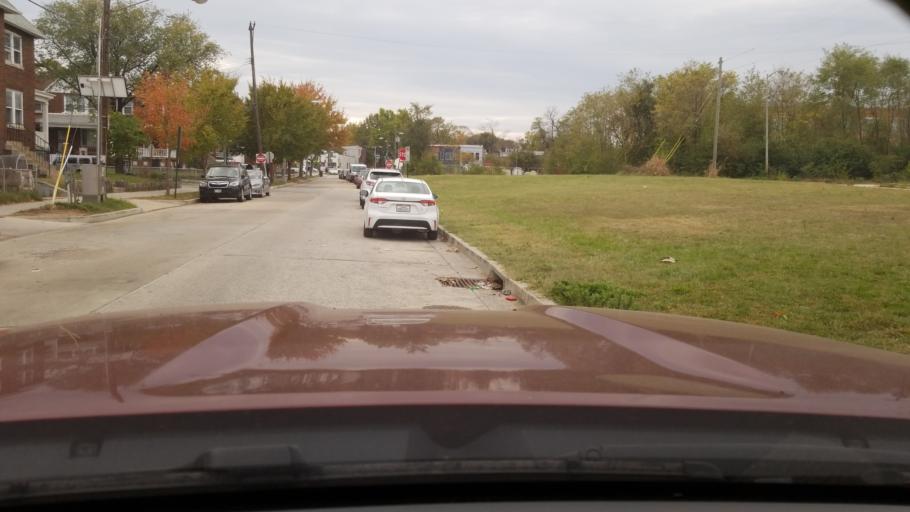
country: US
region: Maryland
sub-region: Prince George's County
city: Hillcrest Heights
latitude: 38.8687
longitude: -76.9871
